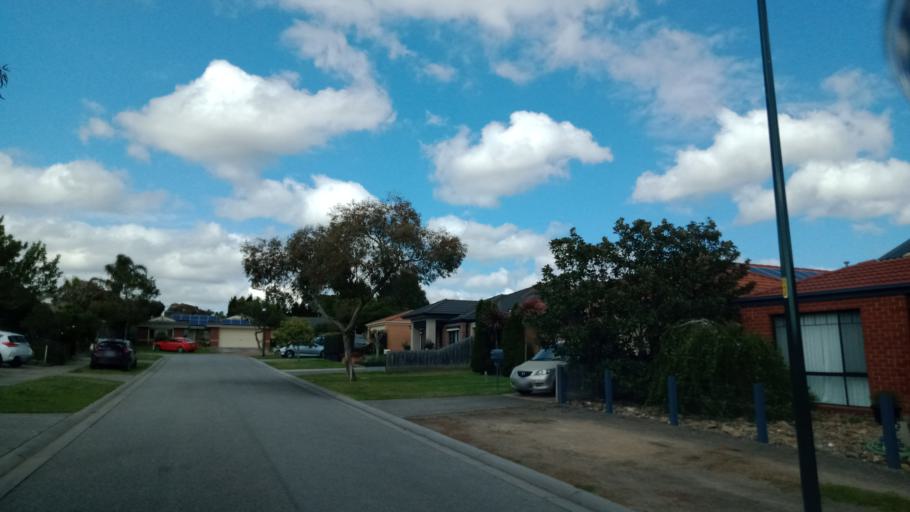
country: AU
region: Victoria
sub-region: Frankston
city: Sandhurst
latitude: -38.0892
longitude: 145.1898
